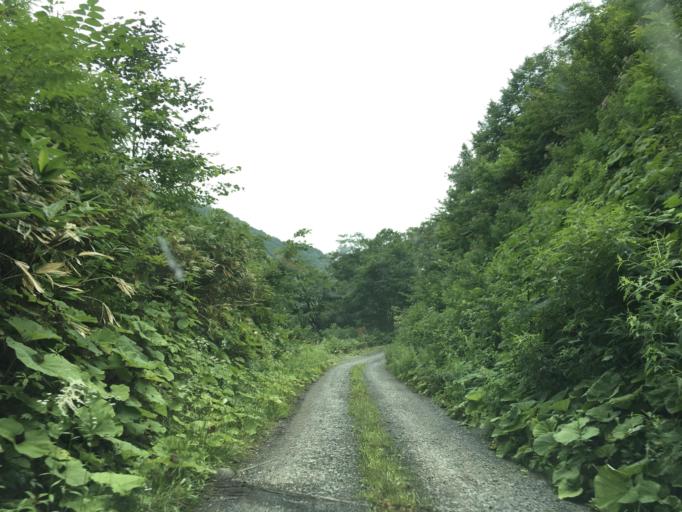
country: JP
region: Iwate
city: Ichinoseki
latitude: 38.9610
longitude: 140.8456
